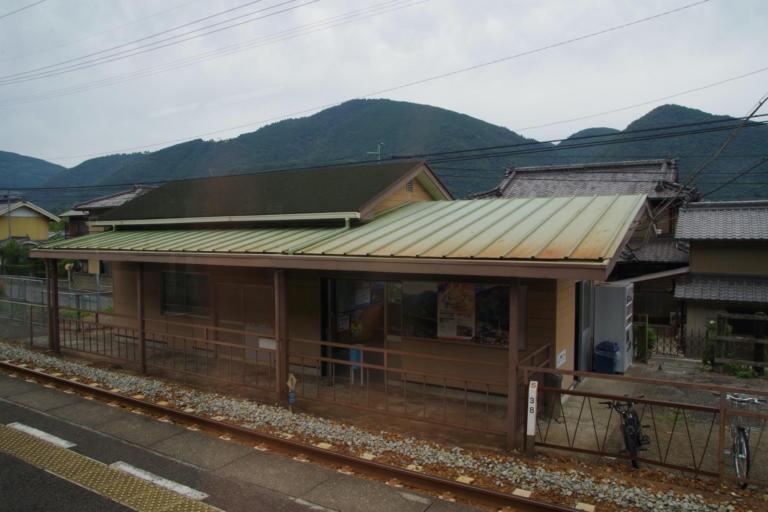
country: JP
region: Tokushima
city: Ikedacho
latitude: 34.0324
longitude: 133.8573
